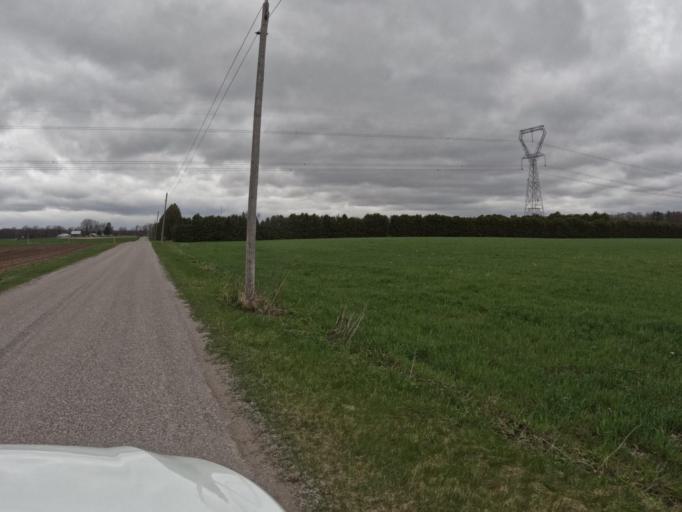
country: CA
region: Ontario
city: Norfolk County
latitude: 42.9577
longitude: -80.4258
